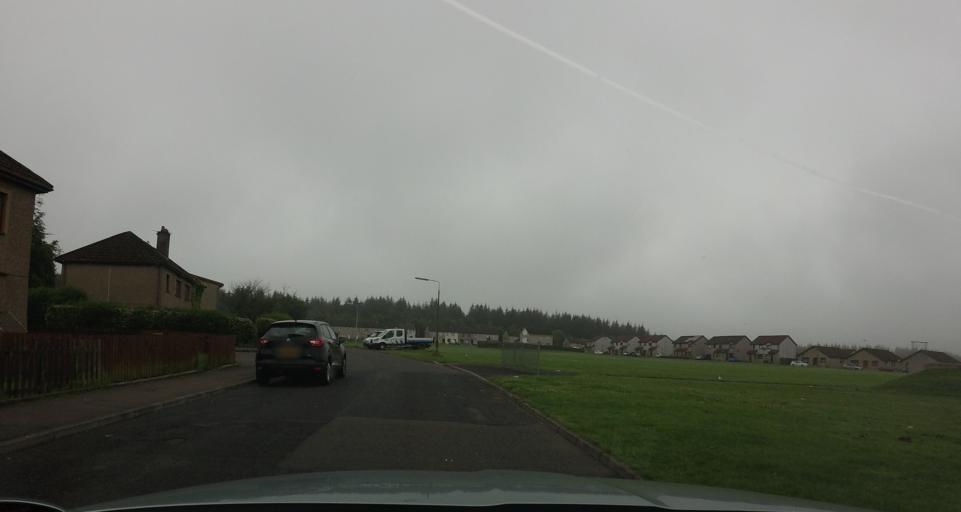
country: GB
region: Scotland
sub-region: Fife
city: Kelty
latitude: 56.1351
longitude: -3.3925
